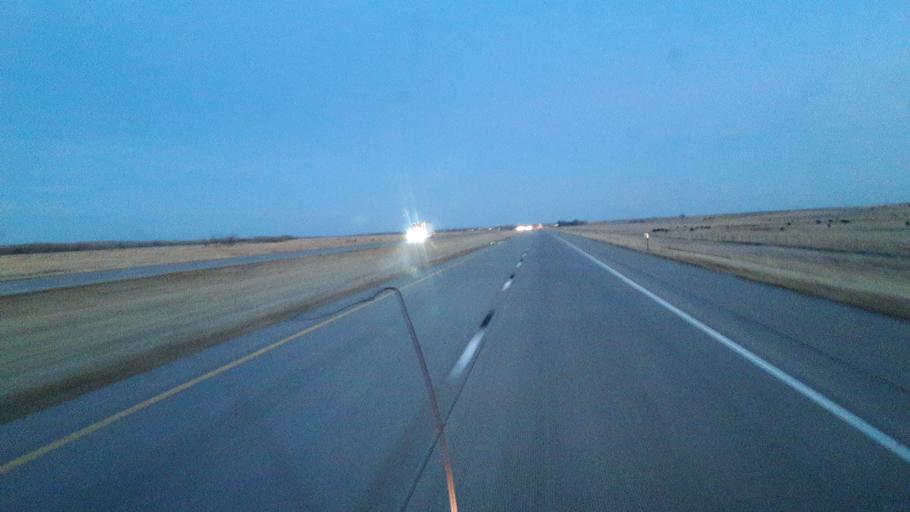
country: US
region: Nebraska
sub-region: Keith County
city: Ogallala
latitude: 41.1120
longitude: -101.5184
